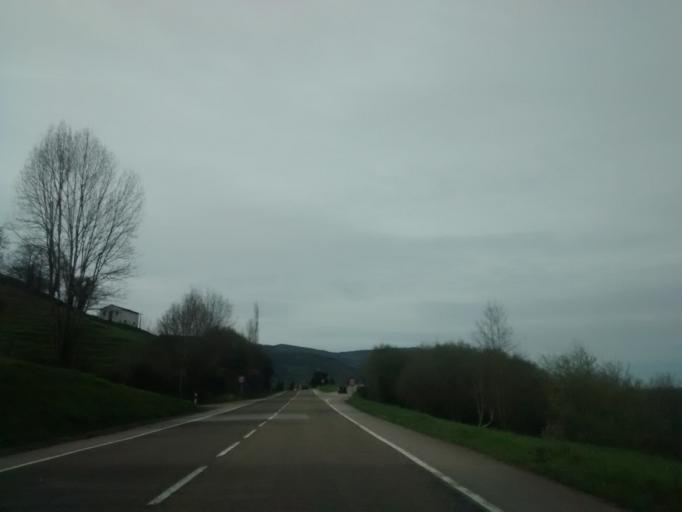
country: ES
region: Cantabria
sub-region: Provincia de Cantabria
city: Santiurde de Toranzo
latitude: 43.2056
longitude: -3.9329
